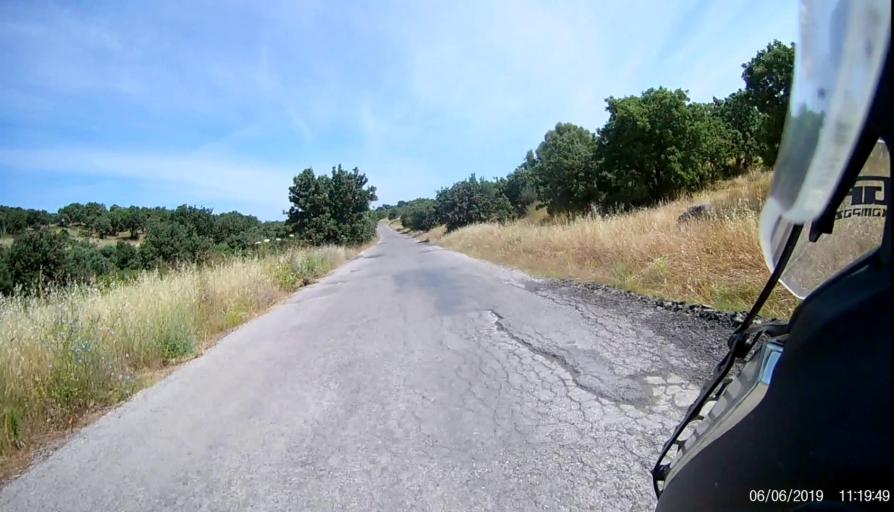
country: TR
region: Canakkale
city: Gulpinar
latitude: 39.6605
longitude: 26.1641
